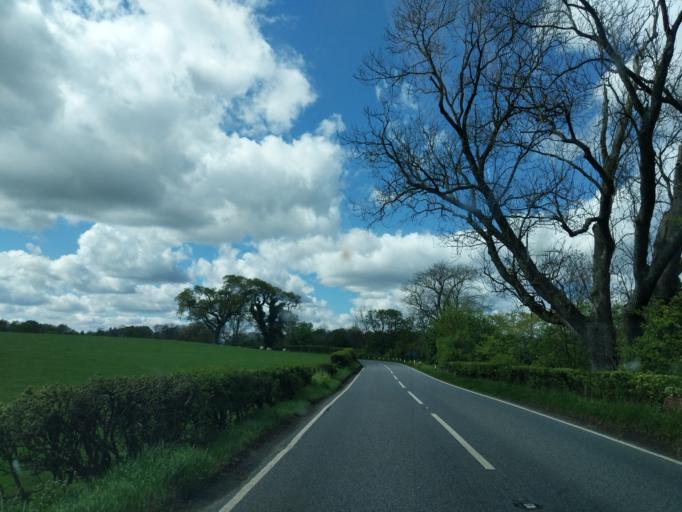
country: GB
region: Scotland
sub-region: Stirling
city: Doune
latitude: 56.1663
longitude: -4.0850
